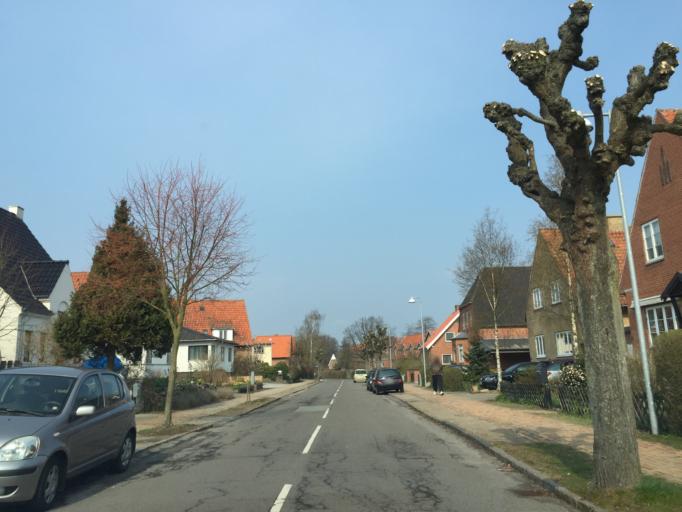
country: DK
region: South Denmark
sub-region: Odense Kommune
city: Odense
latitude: 55.4105
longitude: 10.4020
